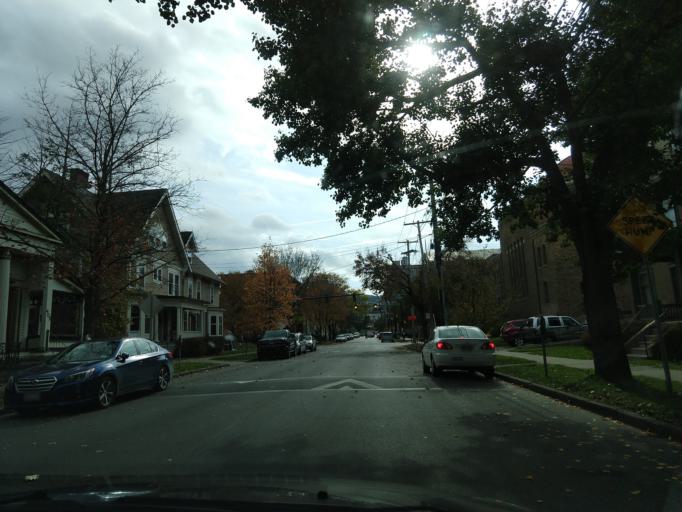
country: US
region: New York
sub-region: Tompkins County
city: Ithaca
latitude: 42.4433
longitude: -76.4970
